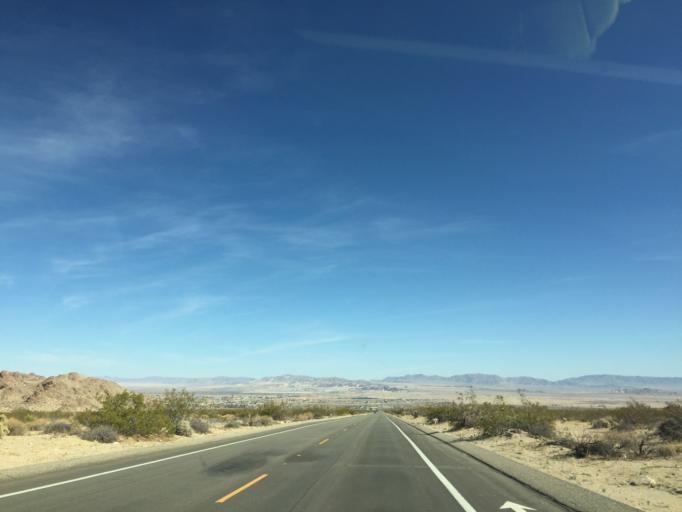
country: US
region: California
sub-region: San Bernardino County
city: Twentynine Palms
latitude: 34.0854
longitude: -116.0366
